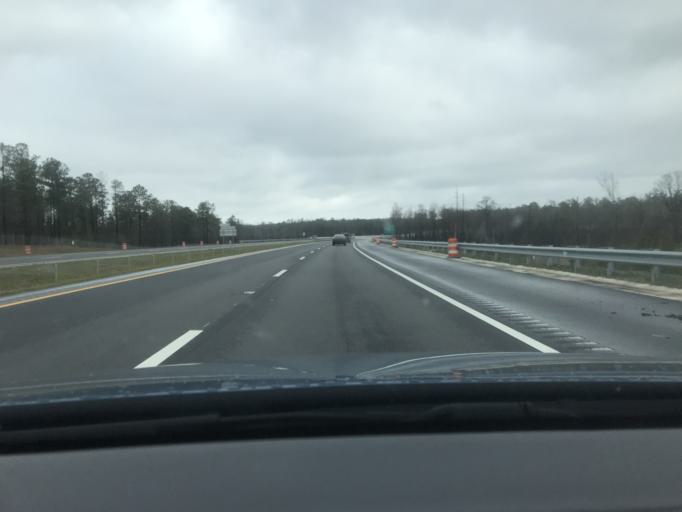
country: US
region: North Carolina
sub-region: Cumberland County
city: Fort Bragg
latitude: 35.0956
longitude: -79.0257
